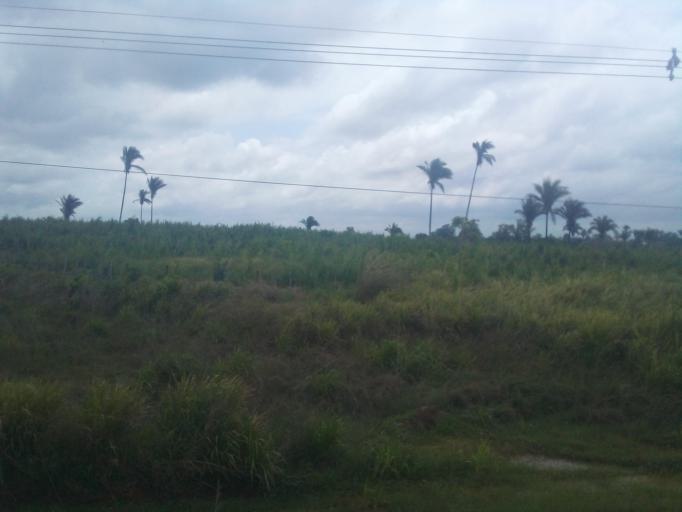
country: BR
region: Maranhao
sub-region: Santa Ines
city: Santa Ines
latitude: -3.6824
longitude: -45.3377
